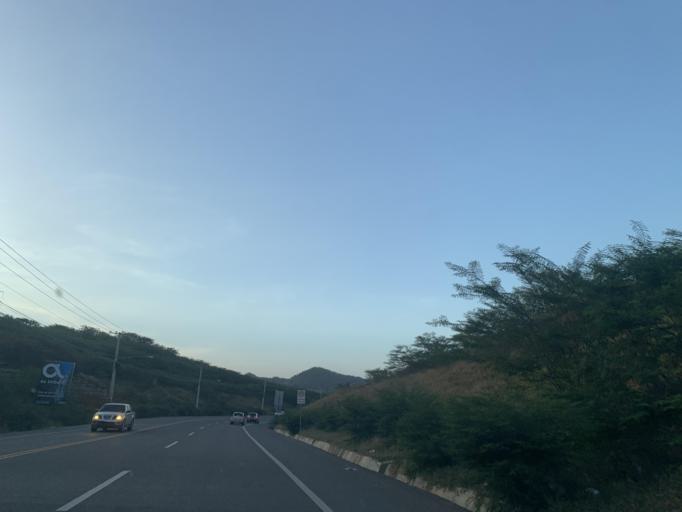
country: DO
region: Puerto Plata
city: Imbert
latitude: 19.7503
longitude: -70.8403
